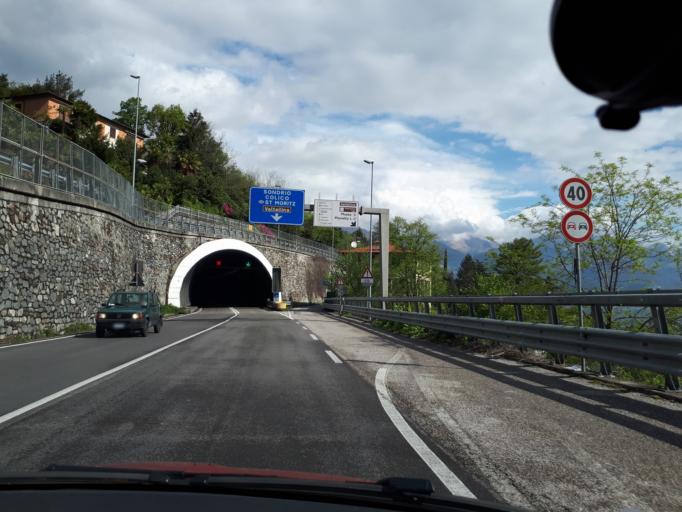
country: IT
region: Lombardy
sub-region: Provincia di Como
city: Vignola
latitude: 46.0912
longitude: 9.2791
